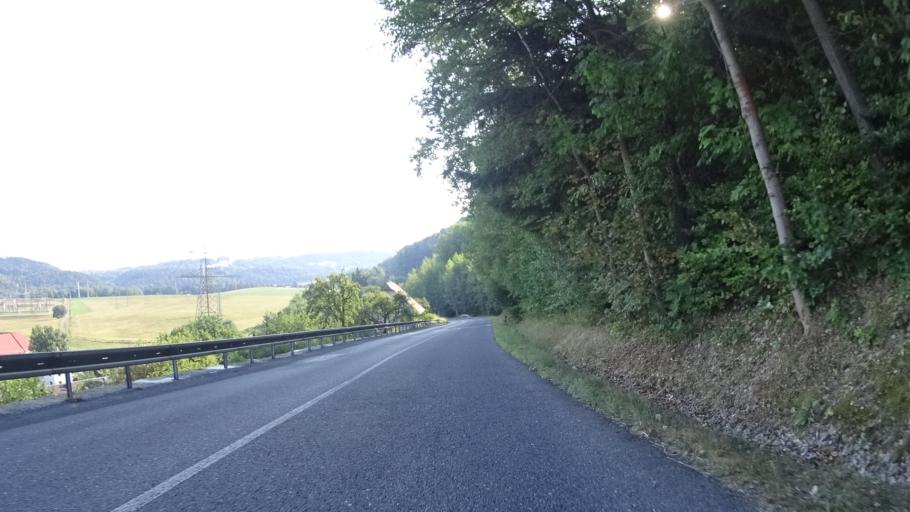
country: CZ
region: Liberecky
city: Hodkovice nad Mohelkou
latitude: 50.6516
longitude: 15.1088
